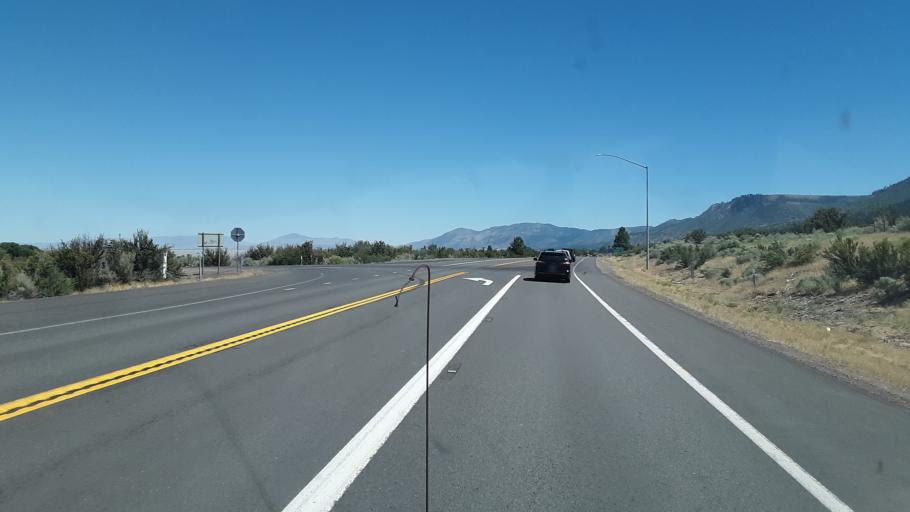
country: US
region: California
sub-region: Lassen County
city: Janesville
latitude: 40.2840
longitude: -120.4907
